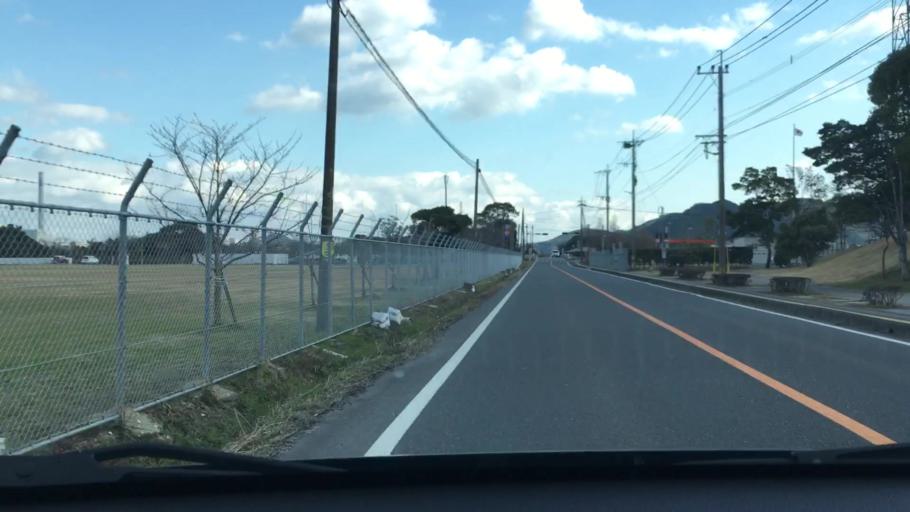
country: JP
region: Oita
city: Saiki
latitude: 32.9697
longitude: 131.9130
